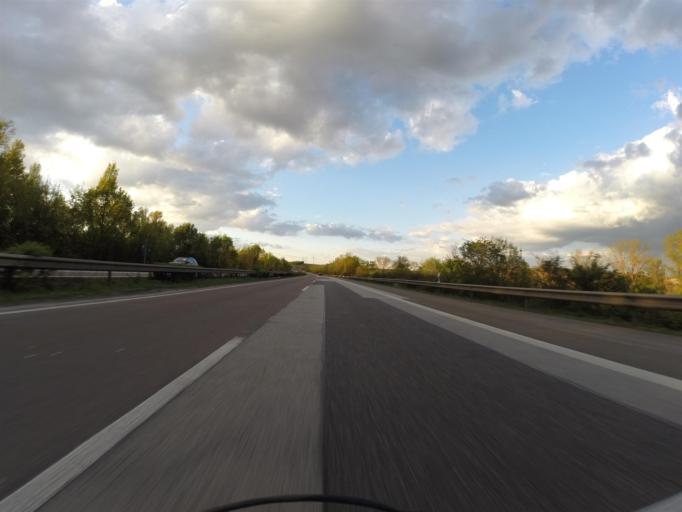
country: DE
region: Rheinland-Pfalz
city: Spiesheim
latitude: 49.8012
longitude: 8.1437
